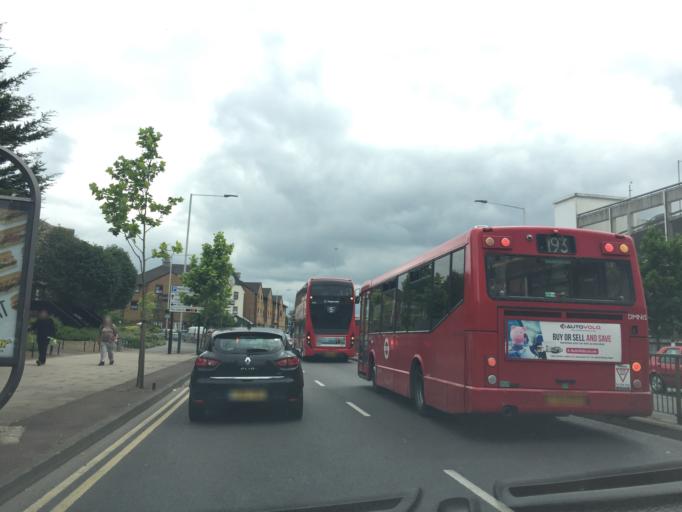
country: GB
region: England
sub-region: Greater London
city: Romford
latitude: 51.5788
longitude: 0.1853
